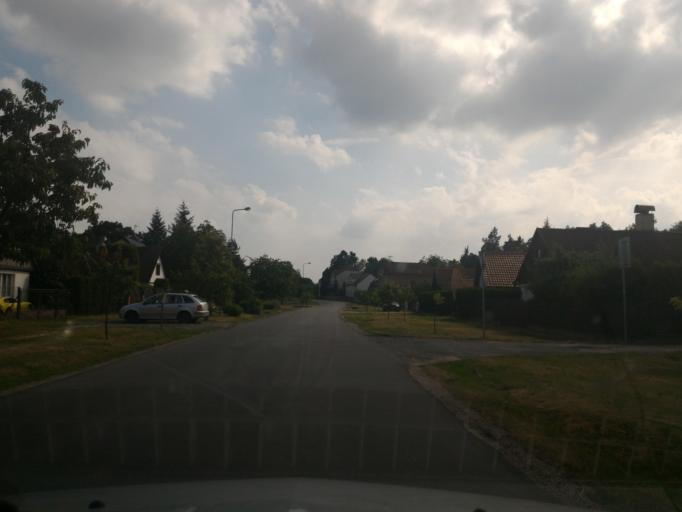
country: CZ
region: Central Bohemia
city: Loucen
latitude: 50.2830
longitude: 15.0186
